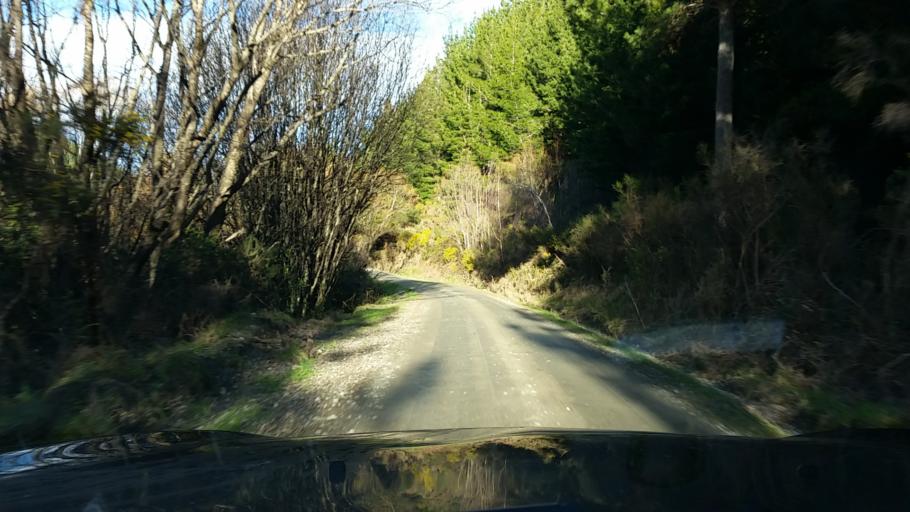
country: NZ
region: Nelson
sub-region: Nelson City
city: Nelson
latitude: -41.5544
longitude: 173.4254
